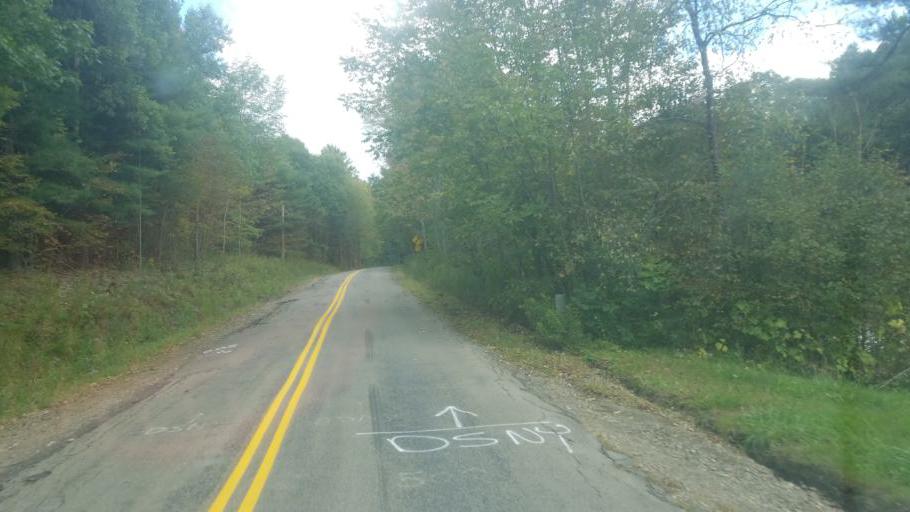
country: US
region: New York
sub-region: Allegany County
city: Cuba
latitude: 42.2212
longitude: -78.3599
